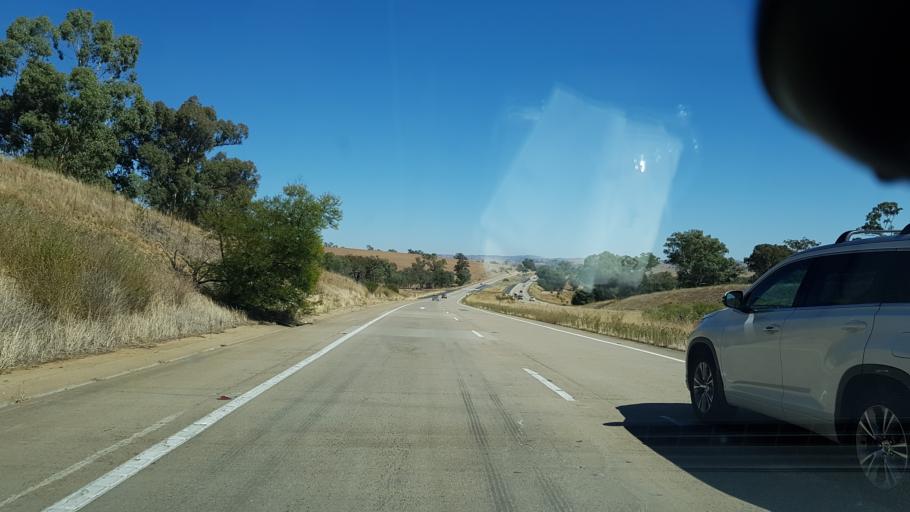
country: AU
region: New South Wales
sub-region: Gundagai
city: Gundagai
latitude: -34.8144
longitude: 148.4103
